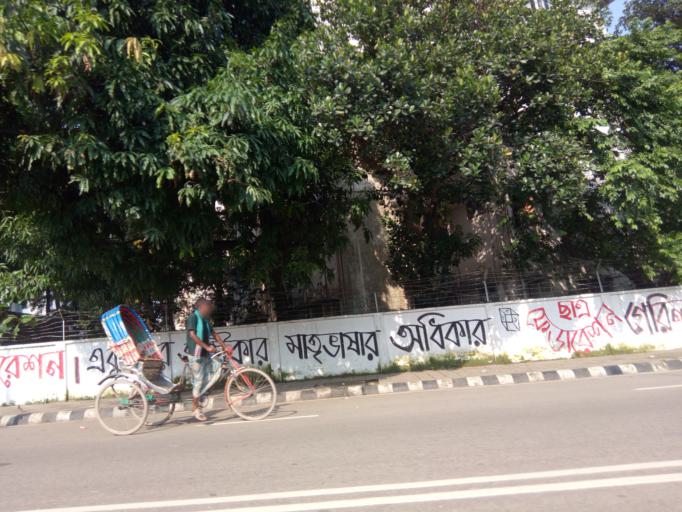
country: BD
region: Dhaka
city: Azimpur
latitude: 23.7287
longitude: 90.3953
